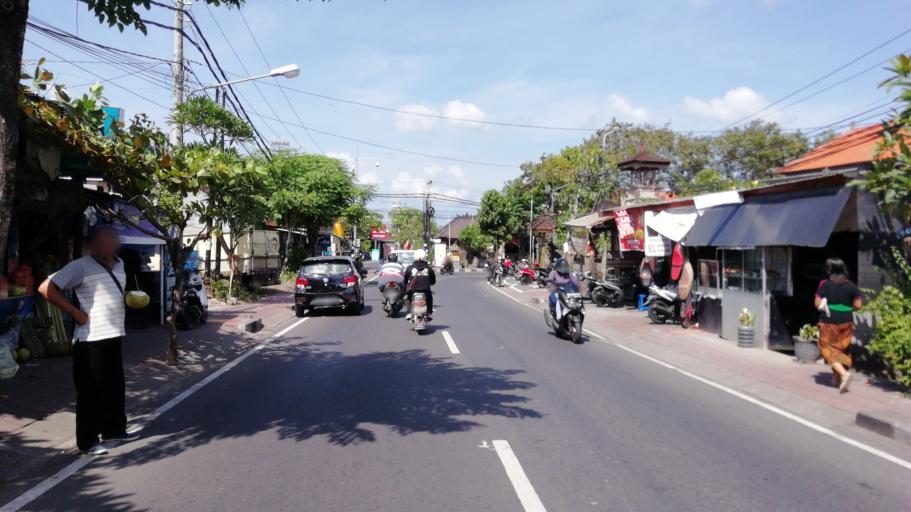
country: ID
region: Bali
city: Banjar Gunungpande
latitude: -8.6464
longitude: 115.1681
